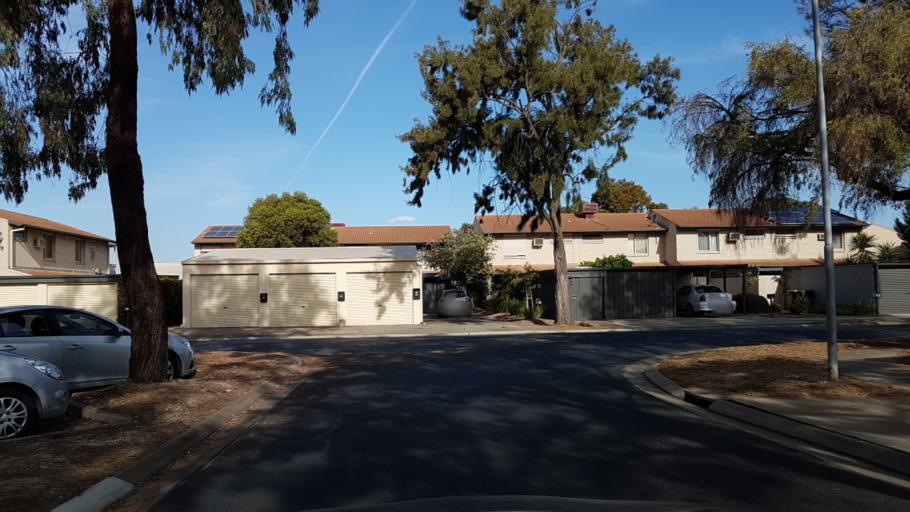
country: AU
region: South Australia
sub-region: Charles Sturt
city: West Lakes Shore
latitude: -34.8557
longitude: 138.4970
